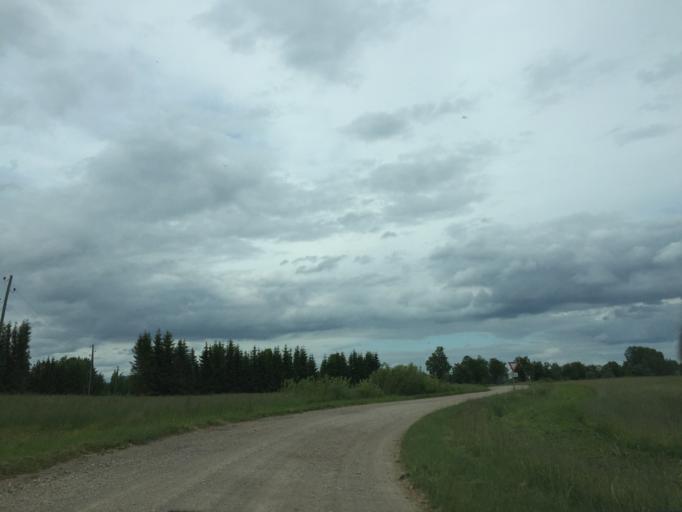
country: LV
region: Apes Novads
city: Ape
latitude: 57.4528
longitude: 26.3558
